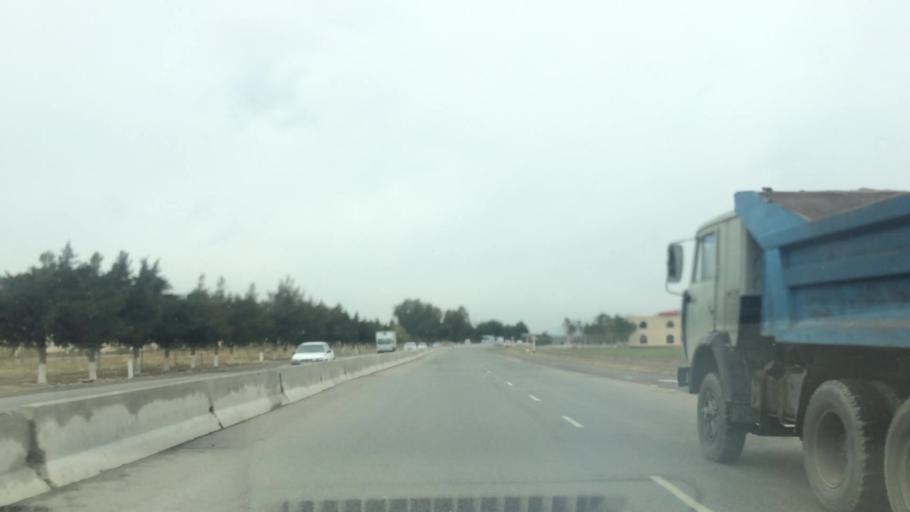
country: UZ
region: Samarqand
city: Bulung'ur
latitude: 39.7593
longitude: 67.2501
